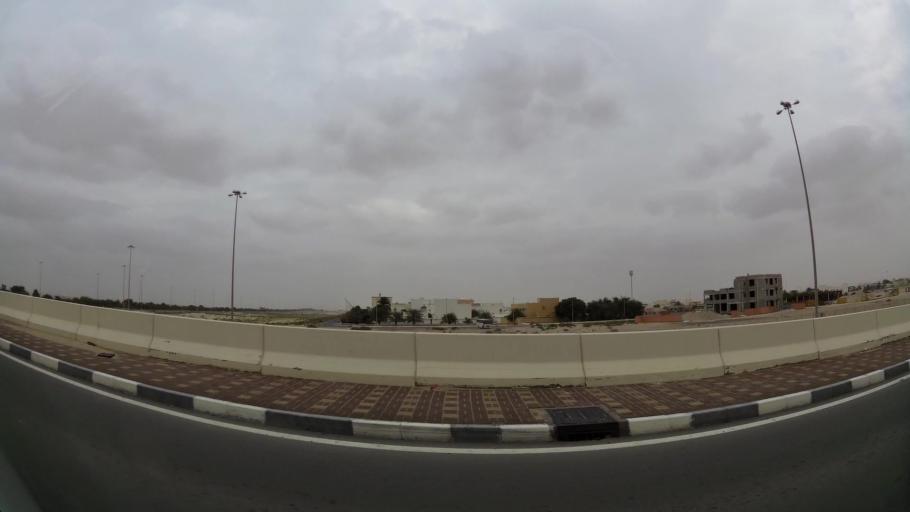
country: AE
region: Abu Dhabi
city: Abu Dhabi
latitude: 24.3682
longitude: 54.6566
